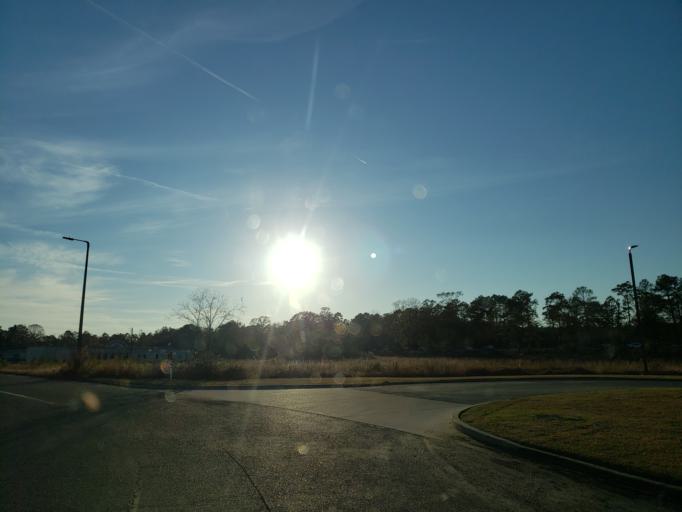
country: US
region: Mississippi
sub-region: Lamar County
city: Arnold Line
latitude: 31.3532
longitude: -89.3477
